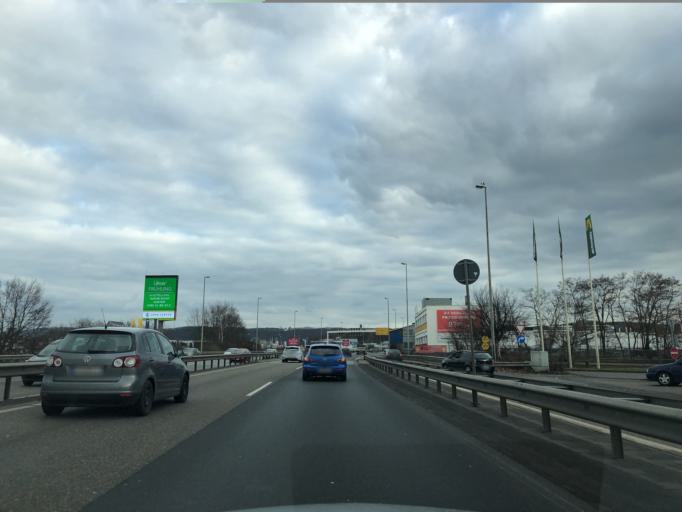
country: DE
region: Rheinland-Pfalz
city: Koblenz
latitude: 50.3802
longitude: 7.5782
